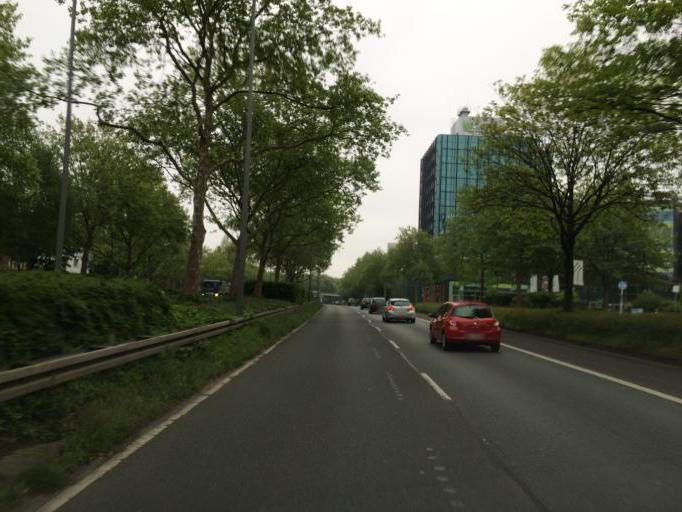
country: DE
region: North Rhine-Westphalia
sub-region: Regierungsbezirk Arnsberg
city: Dortmund
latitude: 51.5012
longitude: 7.4859
